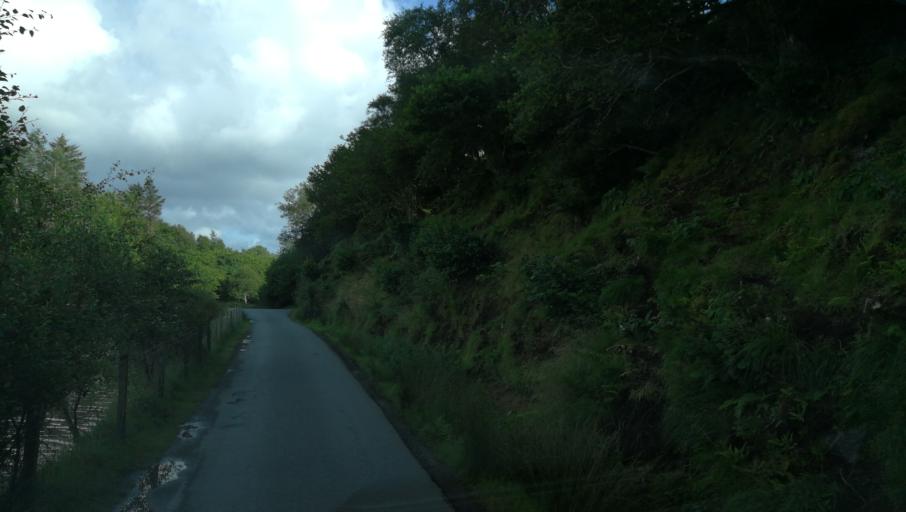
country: GB
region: Scotland
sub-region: Highland
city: Isle of Skye
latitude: 57.4314
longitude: -6.5763
